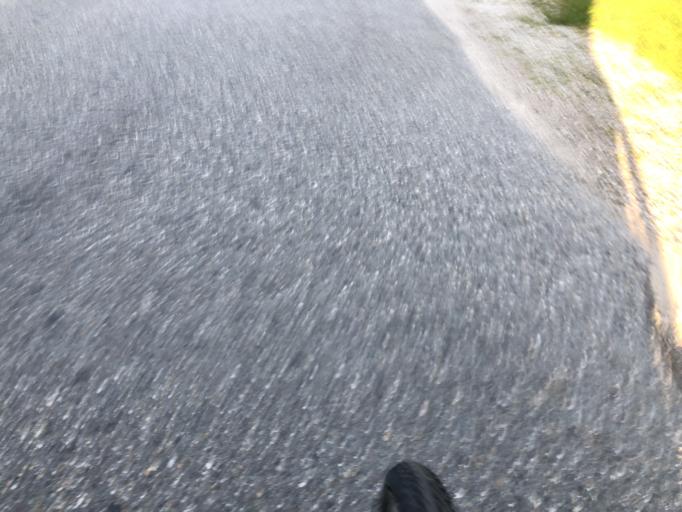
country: CA
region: British Columbia
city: Richmond
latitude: 49.1418
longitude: -123.1334
